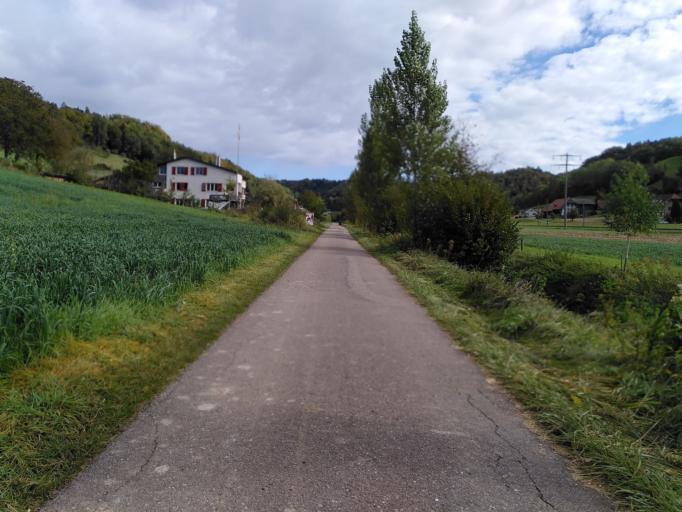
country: CH
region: Bern
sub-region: Oberaargau
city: Seeberg
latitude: 47.1362
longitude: 7.6855
